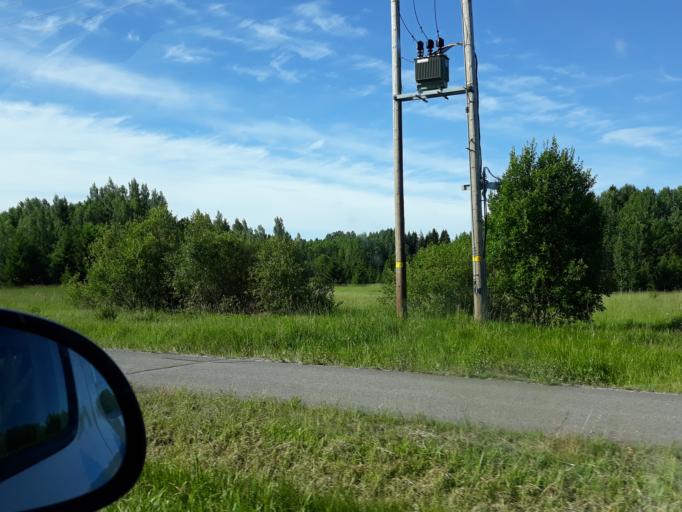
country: FI
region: Uusimaa
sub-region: Helsinki
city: Jaervenpaeae
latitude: 60.5478
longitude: 24.9805
